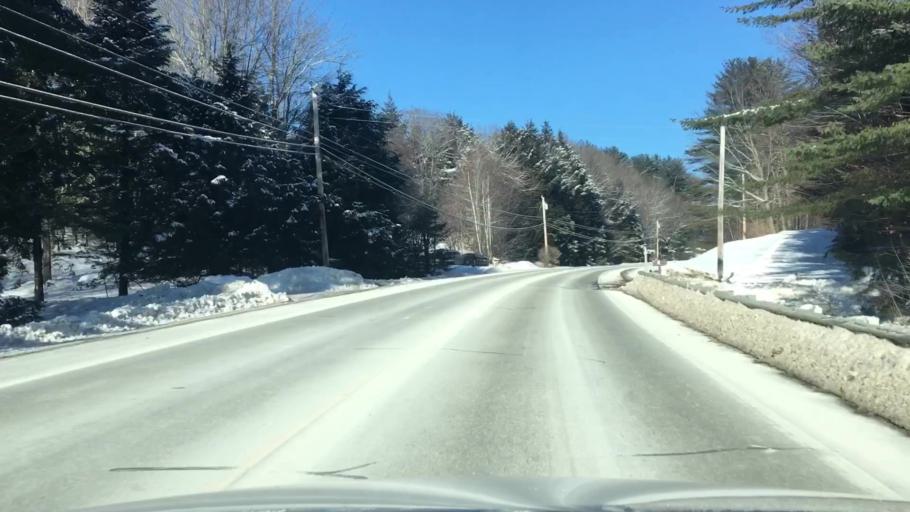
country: US
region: Maine
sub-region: Kennebec County
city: Readfield
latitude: 44.3943
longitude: -69.9890
